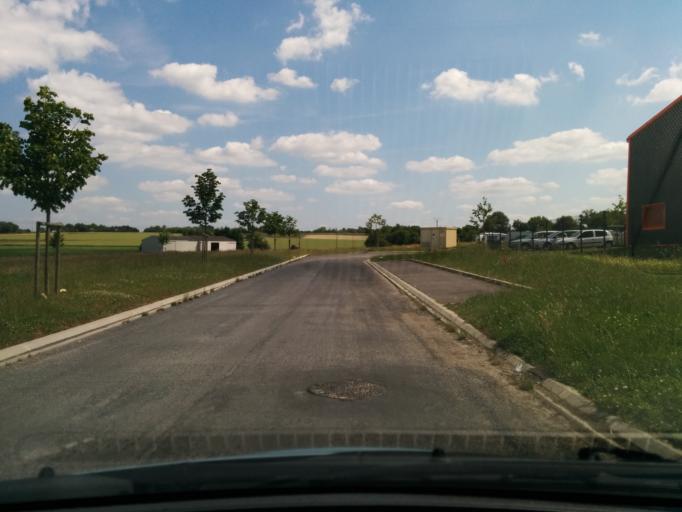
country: FR
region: Ile-de-France
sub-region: Departement des Yvelines
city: Freneuse
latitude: 49.0362
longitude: 1.6046
